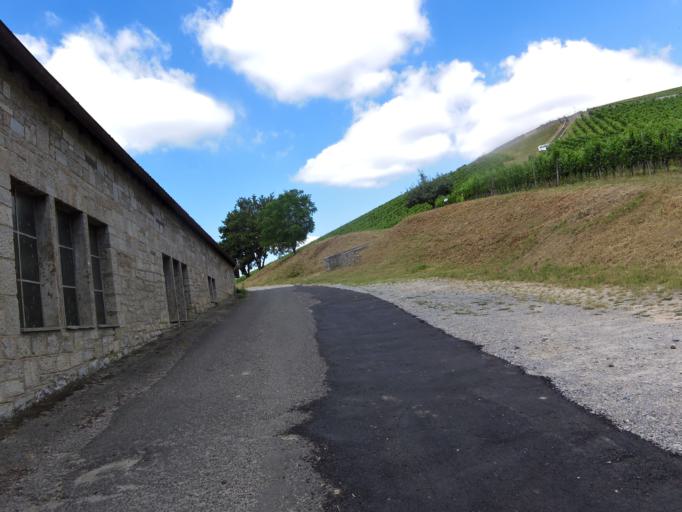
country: DE
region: Bavaria
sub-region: Regierungsbezirk Unterfranken
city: Randersacker
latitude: 49.7677
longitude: 9.9599
